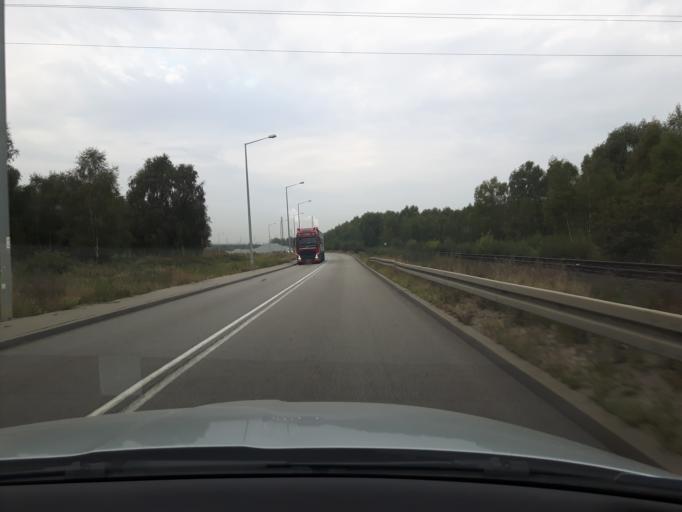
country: PL
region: Pomeranian Voivodeship
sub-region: Gdansk
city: Gdansk
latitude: 54.3796
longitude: 18.6893
